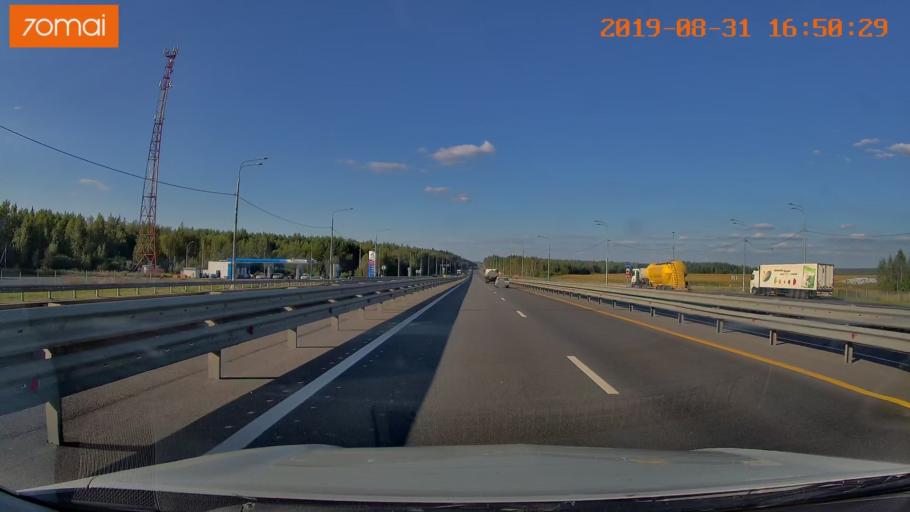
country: RU
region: Kaluga
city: Pyatovskiy
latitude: 54.7094
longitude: 36.1630
